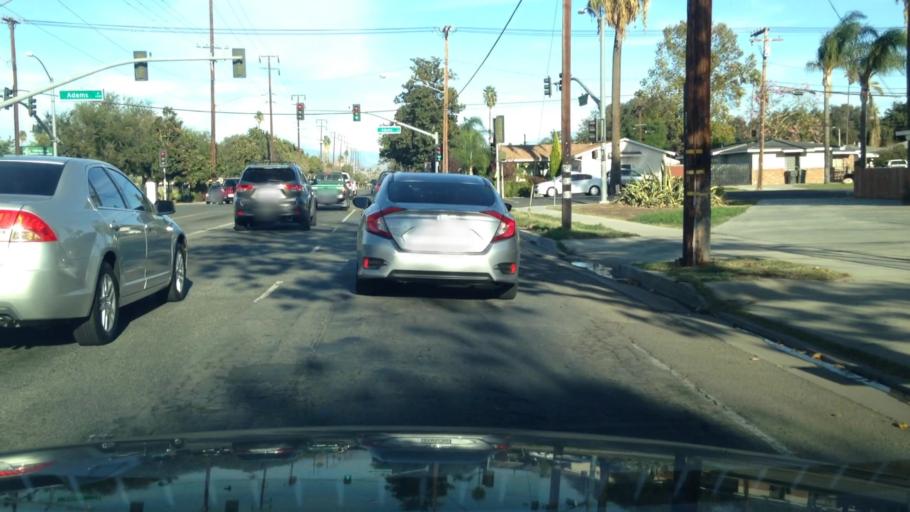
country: US
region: California
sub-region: Riverside County
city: Riverside
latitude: 33.9389
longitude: -117.4299
